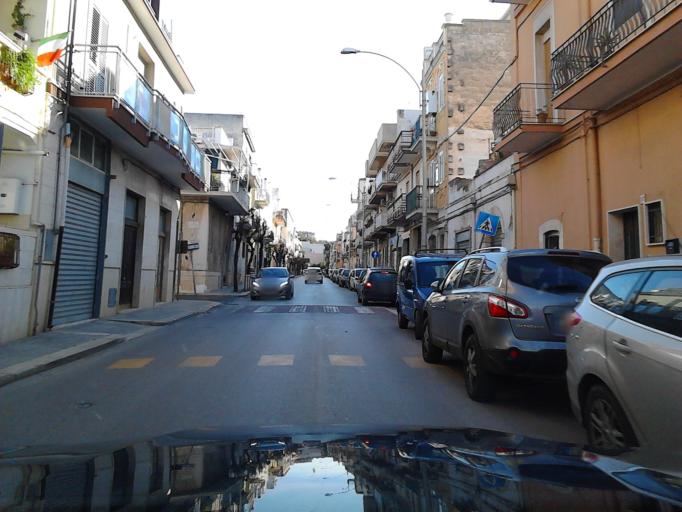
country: IT
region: Apulia
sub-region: Provincia di Bari
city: Rutigliano
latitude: 41.0142
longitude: 17.0015
